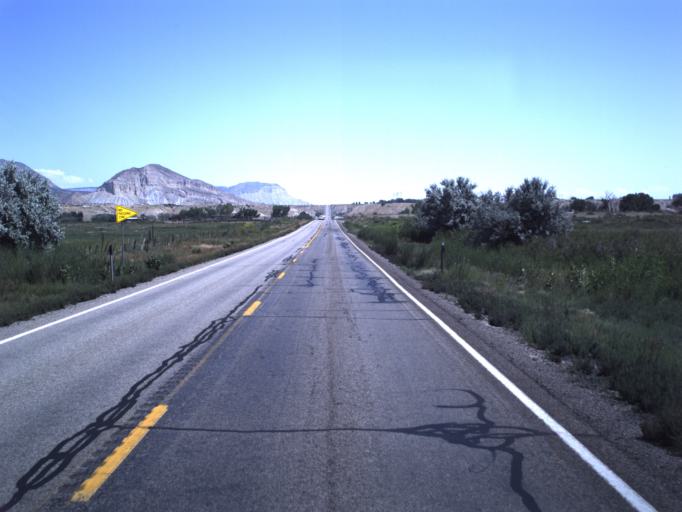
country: US
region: Utah
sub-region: Emery County
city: Ferron
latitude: 38.8672
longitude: -111.2970
